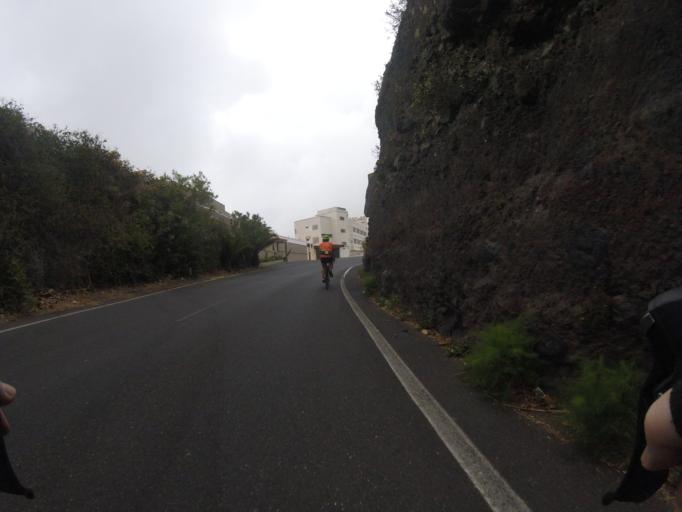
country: ES
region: Canary Islands
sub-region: Provincia de Santa Cruz de Tenerife
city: Guimar
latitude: 28.2944
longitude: -16.4035
